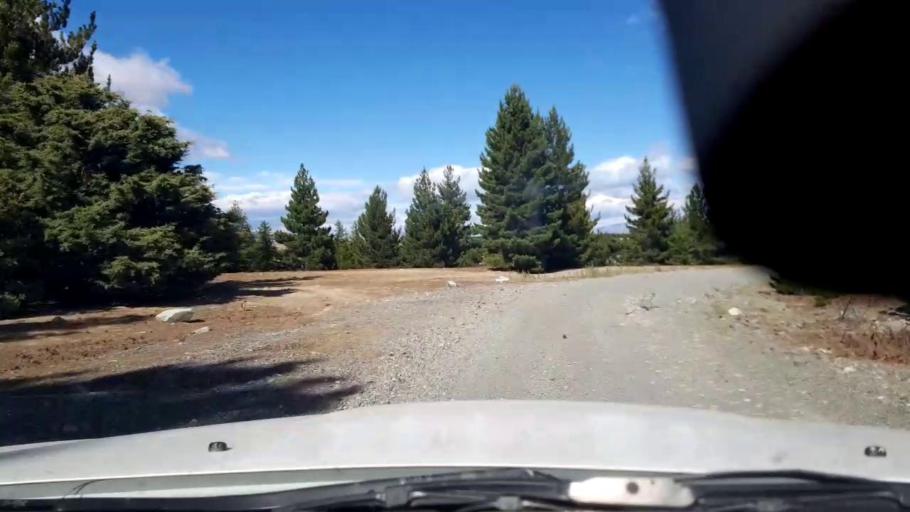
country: NZ
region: Canterbury
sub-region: Timaru District
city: Pleasant Point
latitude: -44.0149
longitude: 170.4716
